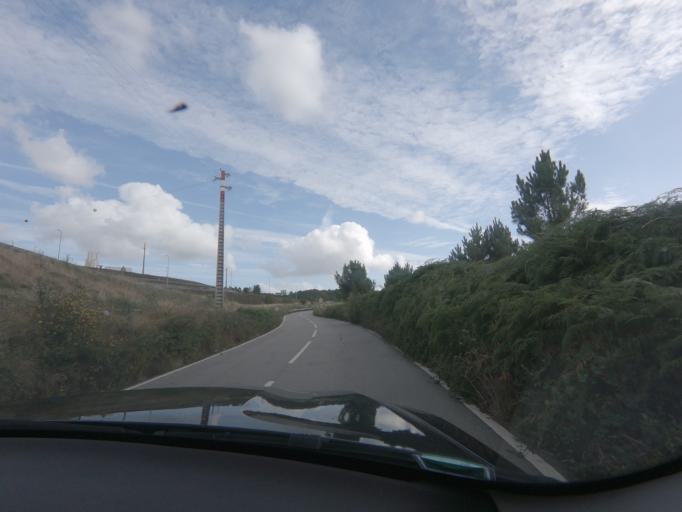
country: PT
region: Vila Real
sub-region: Vila Real
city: Vila Real
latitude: 41.2550
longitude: -7.7158
